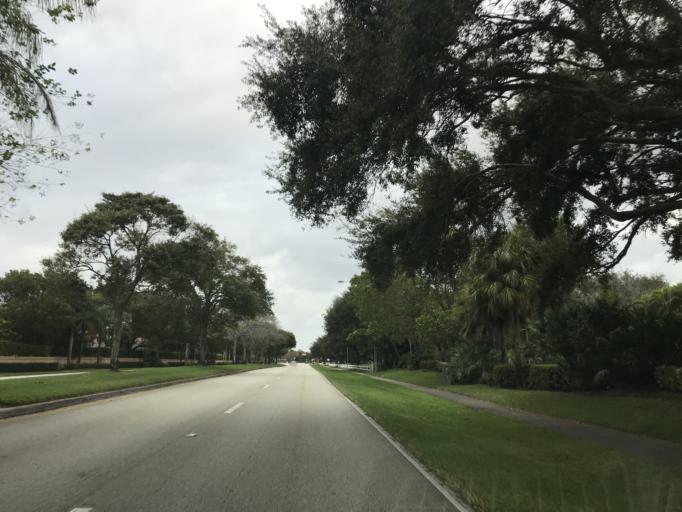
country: US
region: Florida
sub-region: Broward County
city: Parkland
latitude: 26.2981
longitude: -80.2620
